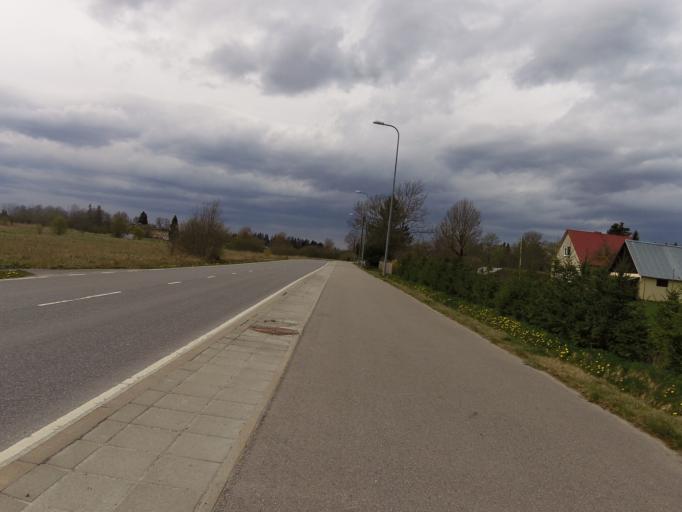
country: EE
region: Harju
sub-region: Rae vald
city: Jueri
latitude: 59.3737
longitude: 24.8420
